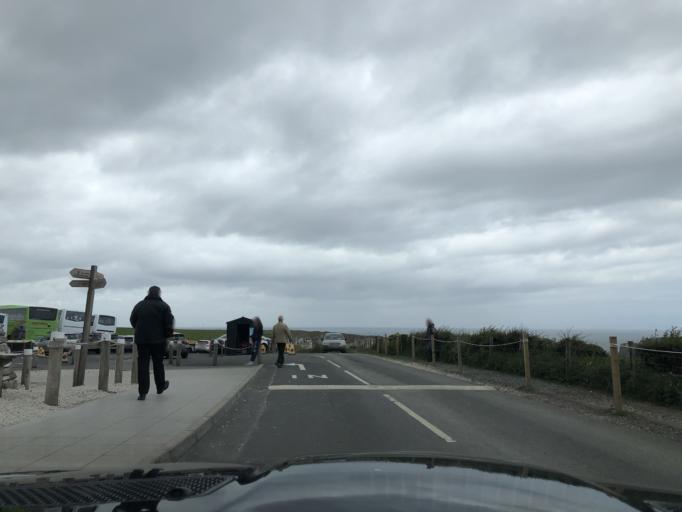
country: GB
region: Northern Ireland
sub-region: Moyle District
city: Ballycastle
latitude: 55.2391
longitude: -6.3474
